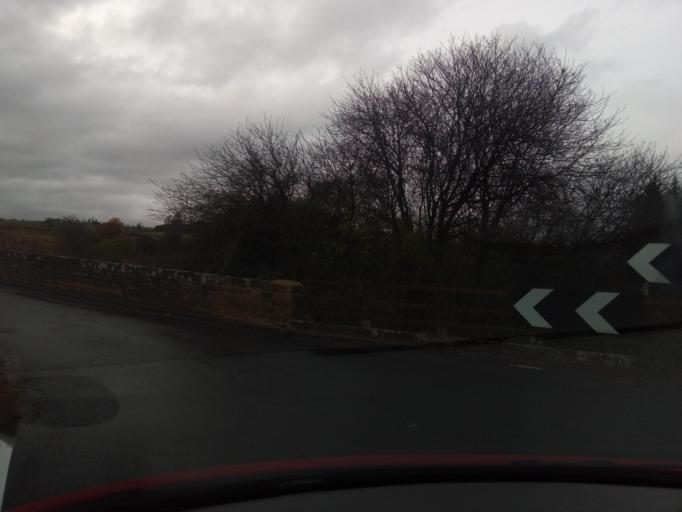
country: GB
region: England
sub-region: County Durham
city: Muggleswick
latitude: 54.8553
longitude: -1.9521
